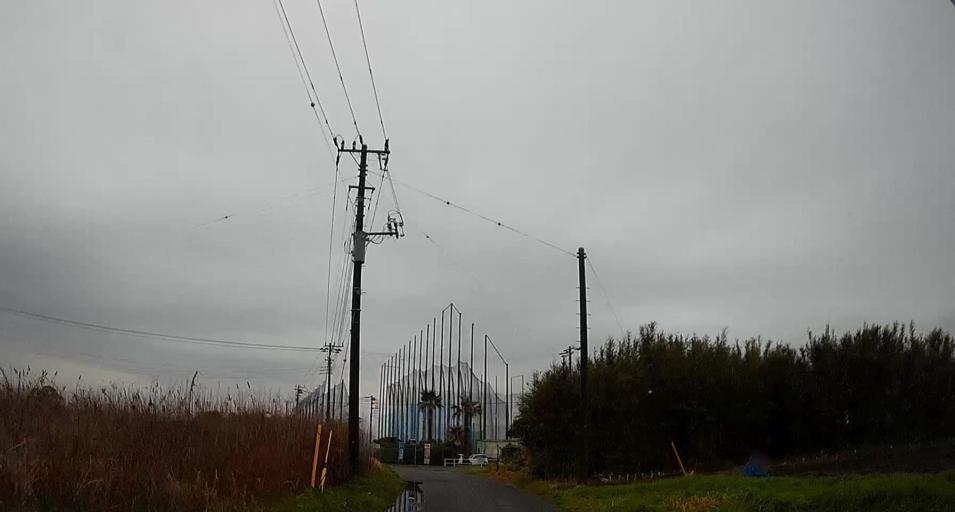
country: JP
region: Chiba
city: Kisarazu
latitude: 35.4085
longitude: 139.9033
